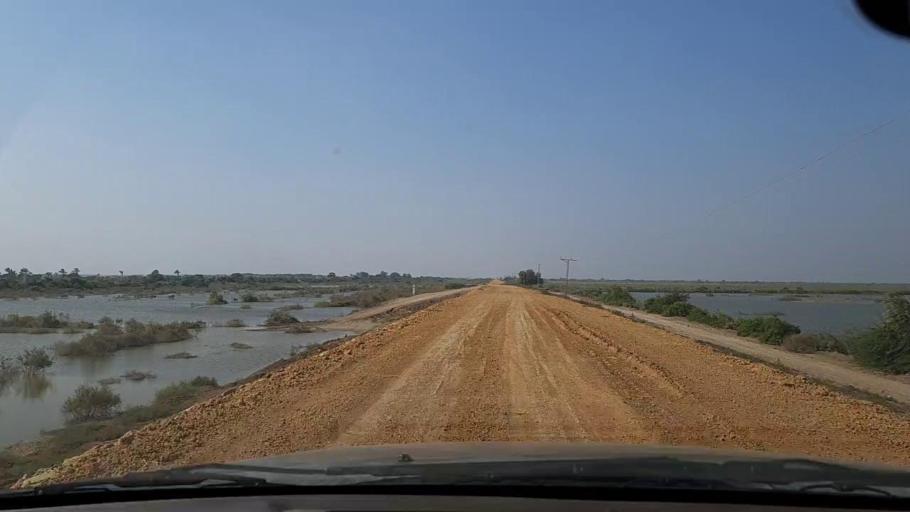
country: PK
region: Sindh
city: Chuhar Jamali
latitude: 24.4610
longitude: 67.9058
